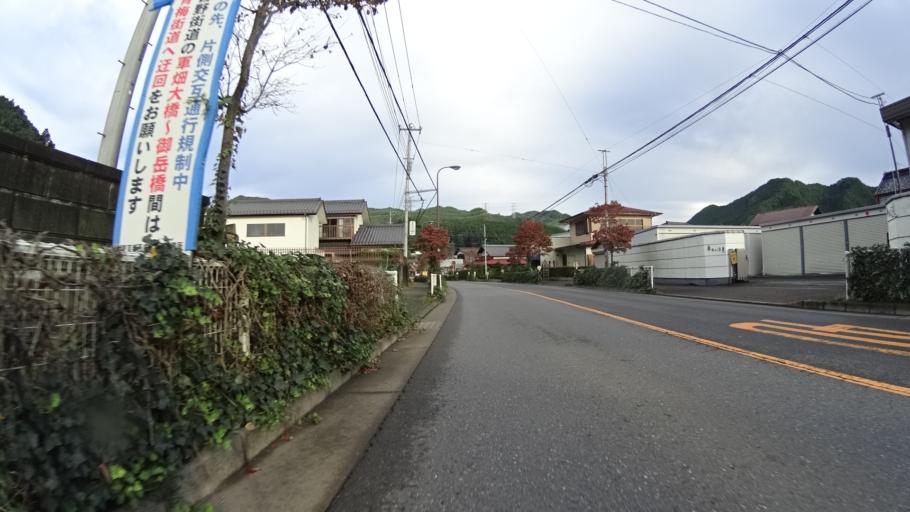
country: JP
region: Tokyo
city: Ome
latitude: 35.8012
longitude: 139.2105
